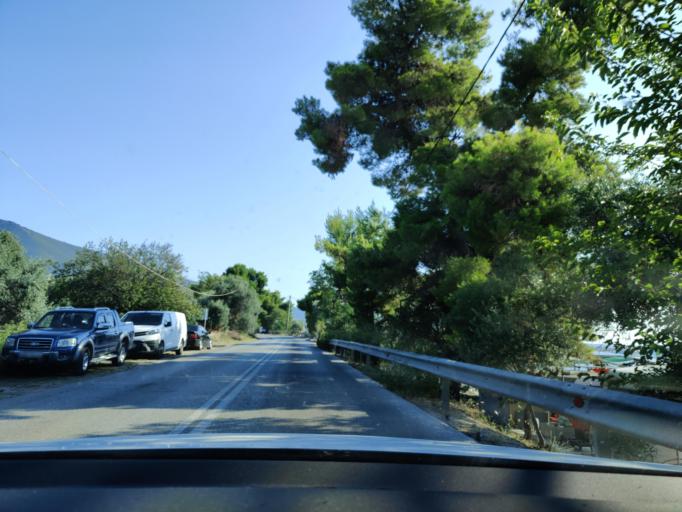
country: GR
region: East Macedonia and Thrace
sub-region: Nomos Kavalas
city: Prinos
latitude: 40.7127
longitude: 24.5343
